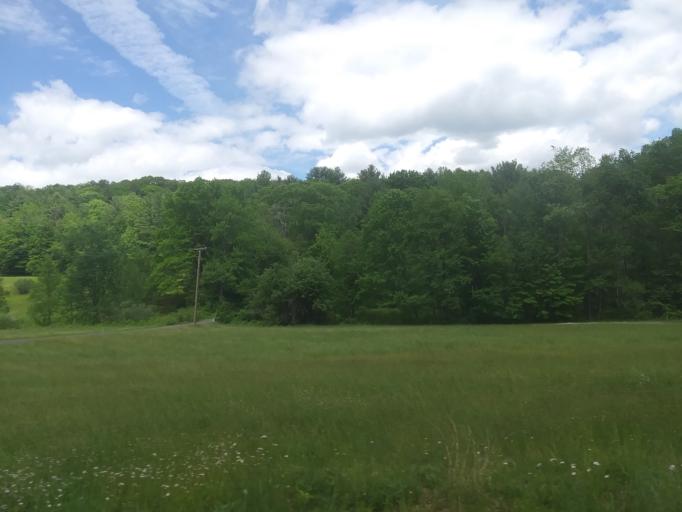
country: US
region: Massachusetts
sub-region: Franklin County
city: Buckland
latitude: 42.5802
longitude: -72.8152
